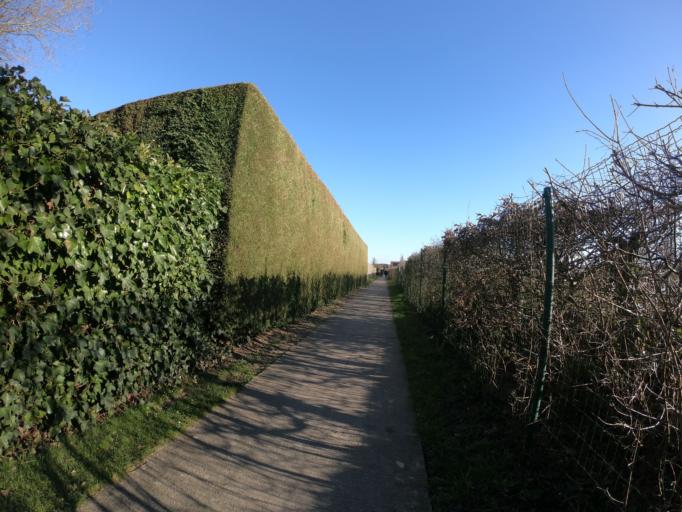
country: BE
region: Flanders
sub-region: Provincie West-Vlaanderen
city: Avelgem
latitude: 50.7803
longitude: 3.4412
